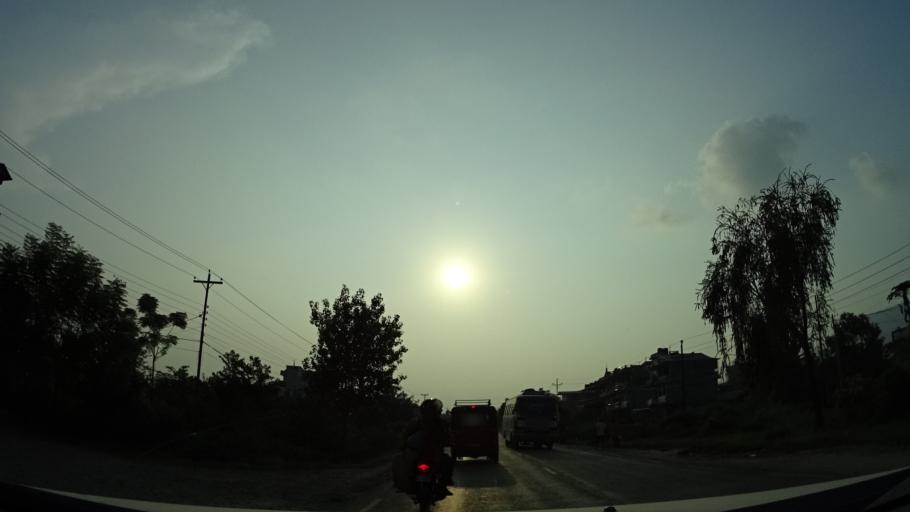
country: NP
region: Central Region
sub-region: Narayani Zone
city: Bharatpur
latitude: 27.6872
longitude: 84.2612
